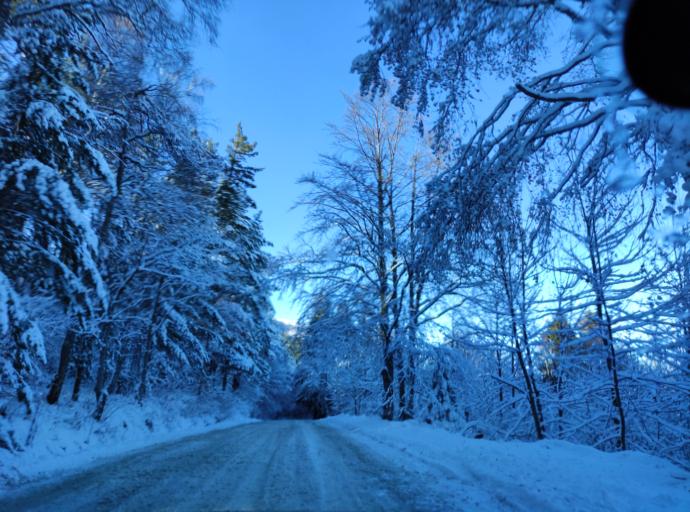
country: BG
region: Sofia-Capital
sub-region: Stolichna Obshtina
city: Sofia
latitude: 42.5950
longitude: 23.3105
